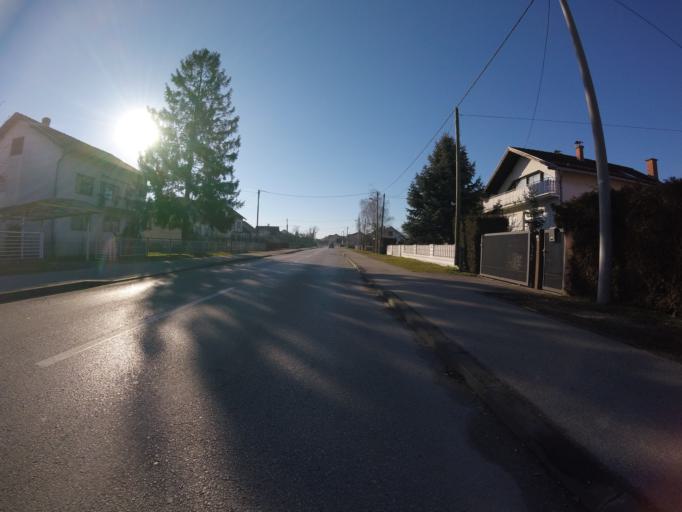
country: HR
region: Zagrebacka
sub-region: Grad Velika Gorica
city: Velika Gorica
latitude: 45.7055
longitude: 16.0755
